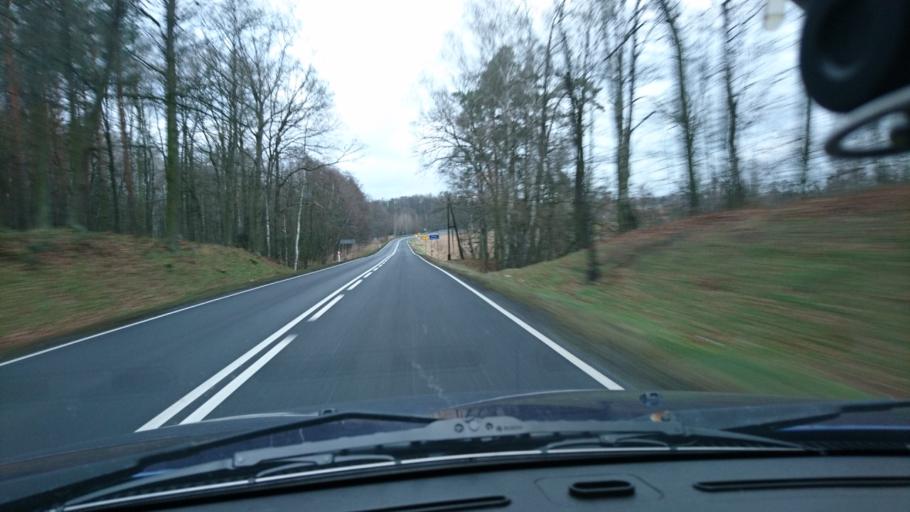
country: PL
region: Opole Voivodeship
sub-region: Powiat kluczborski
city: Kluczbork
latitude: 50.9519
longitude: 18.3112
